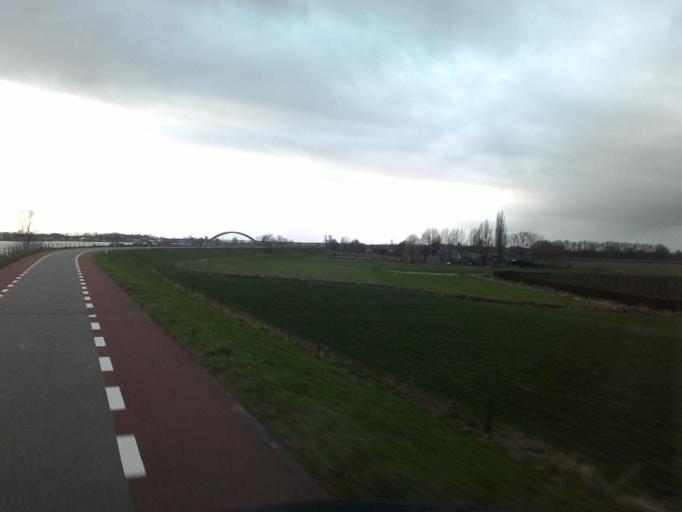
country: NL
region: Gelderland
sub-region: Gemeente Culemborg
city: Culemborg
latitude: 51.9746
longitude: 5.2262
